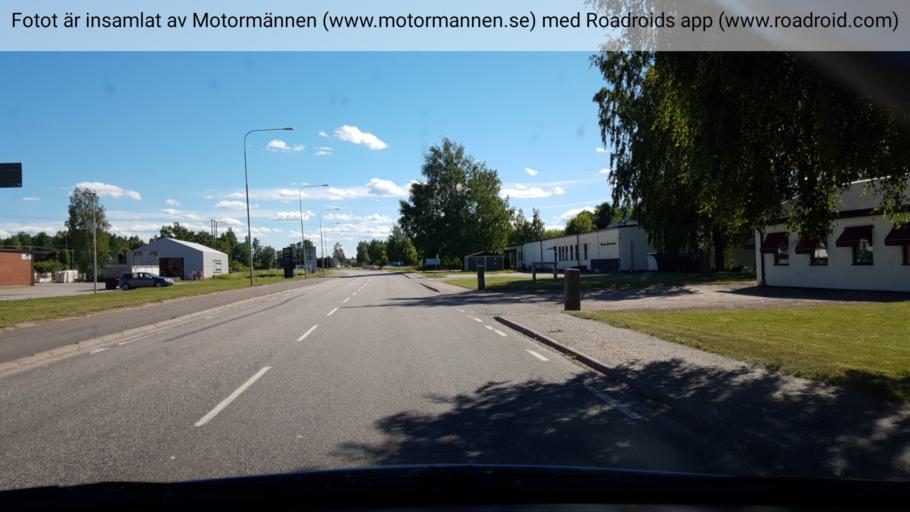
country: SE
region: Vaestra Goetaland
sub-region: Toreboda Kommun
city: Toereboda
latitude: 58.6957
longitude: 14.1171
